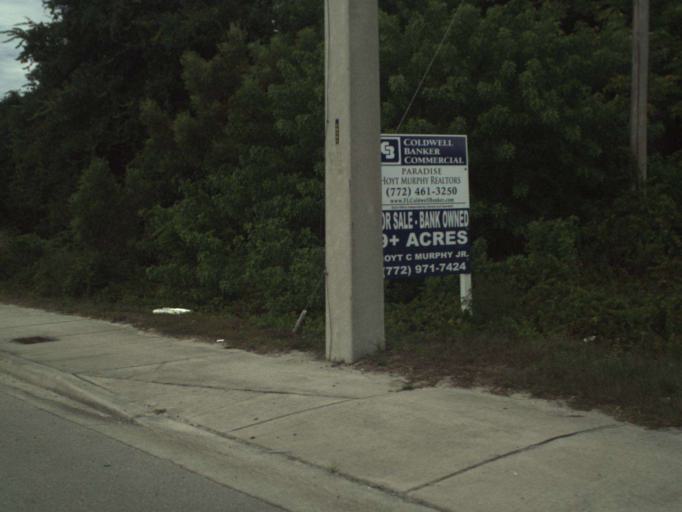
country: US
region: Florida
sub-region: Saint Lucie County
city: Fort Pierce North
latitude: 27.4763
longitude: -80.3498
